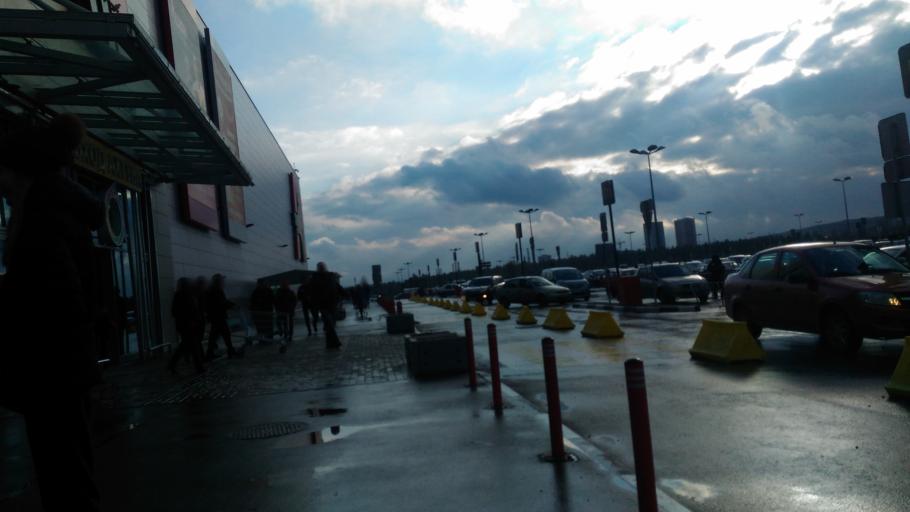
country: RU
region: Volgograd
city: Volgograd
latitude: 48.6361
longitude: 44.4349
